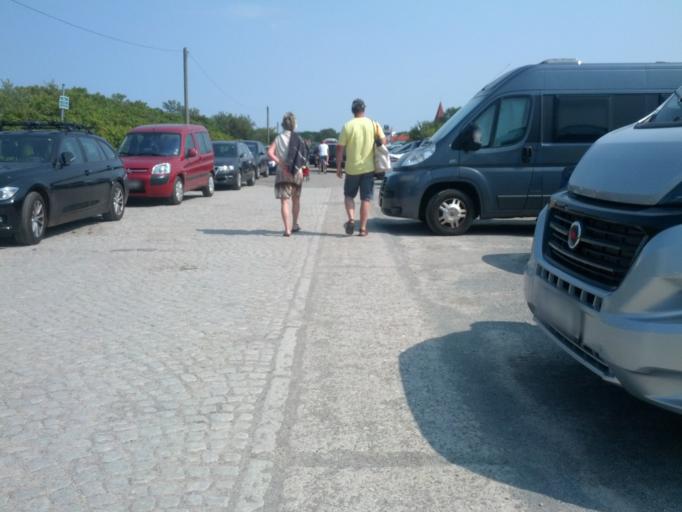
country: DE
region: Mecklenburg-Vorpommern
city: Bastorf
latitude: 54.1029
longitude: 11.6026
